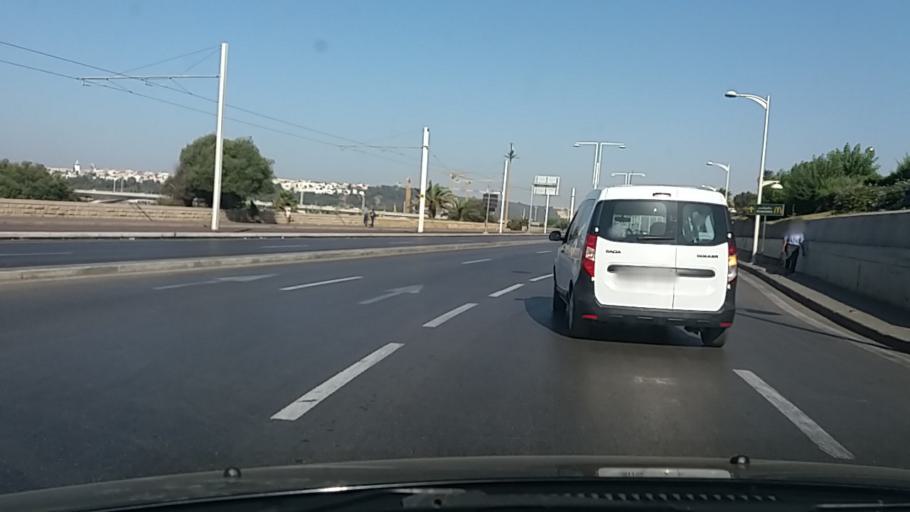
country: MA
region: Rabat-Sale-Zemmour-Zaer
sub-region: Rabat
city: Rabat
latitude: 34.0261
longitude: -6.8250
